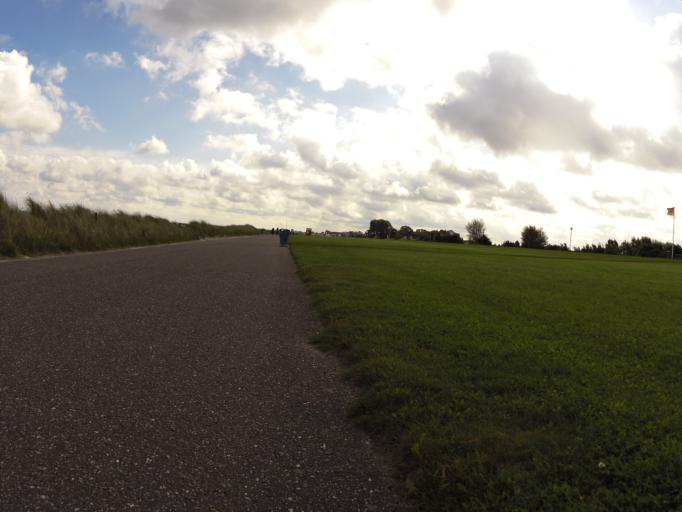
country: DE
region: Schleswig-Holstein
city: Krummbek
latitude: 54.4201
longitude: 10.4033
